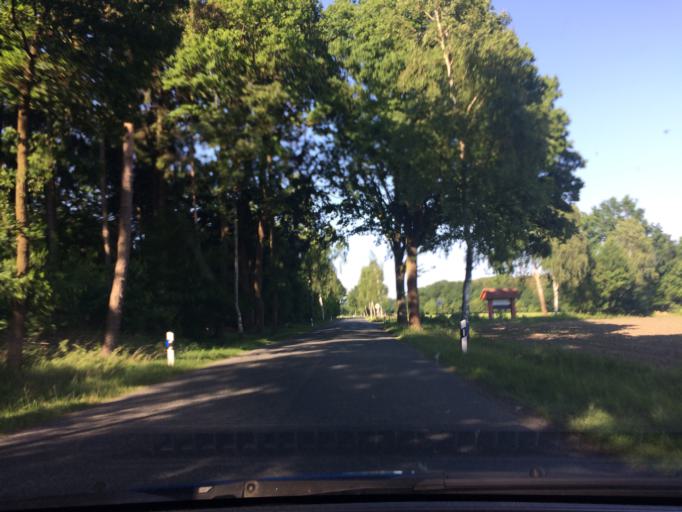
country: DE
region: Lower Saxony
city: Neuenkirchen
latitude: 52.9610
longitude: 9.7053
